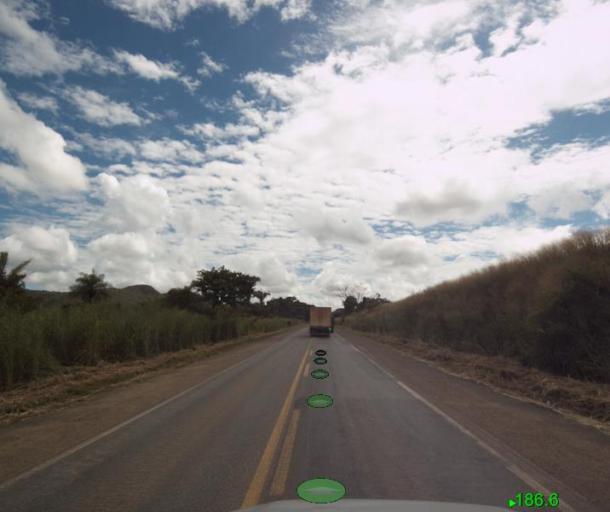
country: BR
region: Goias
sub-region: Uruacu
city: Uruacu
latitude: -14.4086
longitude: -49.1574
